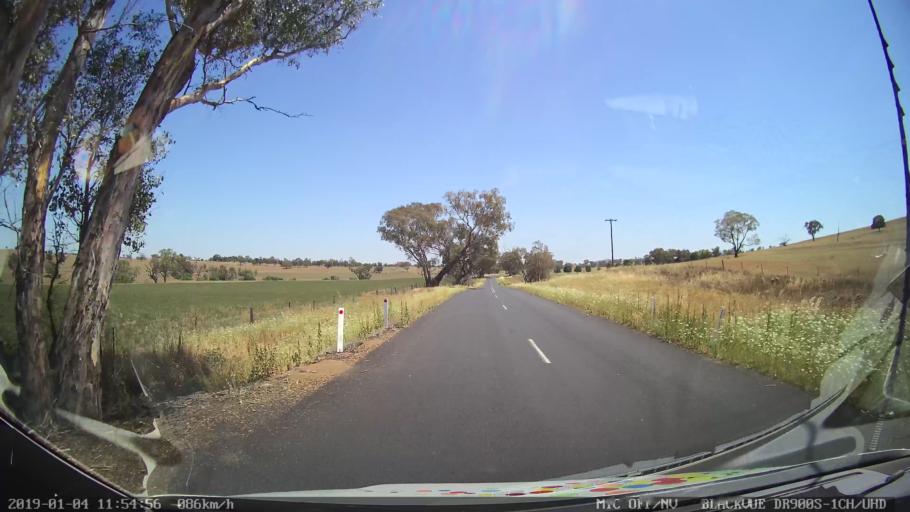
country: AU
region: New South Wales
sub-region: Cabonne
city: Molong
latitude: -32.8600
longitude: 148.7265
